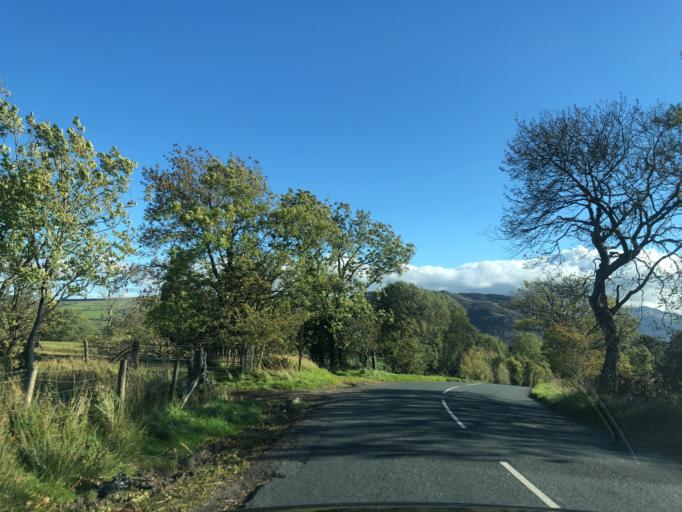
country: GB
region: England
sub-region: Cumbria
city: Ambleside
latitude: 54.6064
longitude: -2.9391
